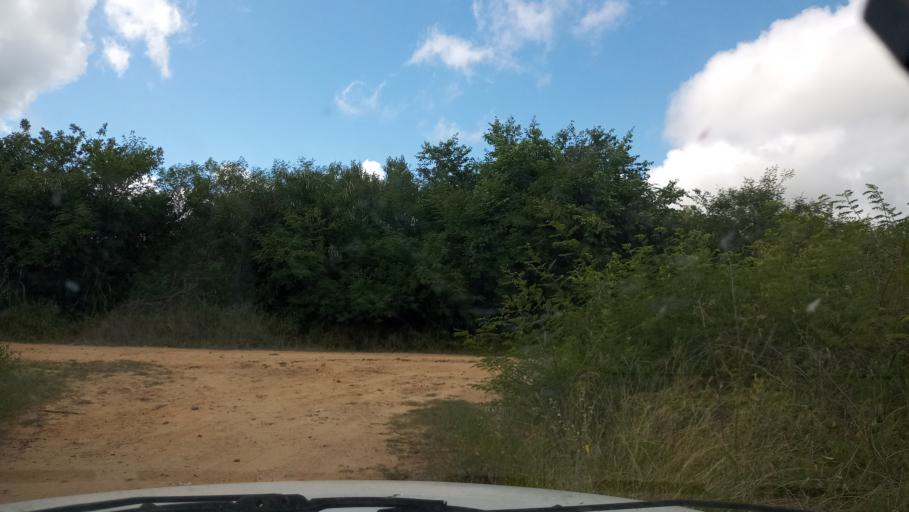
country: BR
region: Rio Grande do Norte
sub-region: Brejinho
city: Brejinho
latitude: -6.1467
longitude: -35.4297
